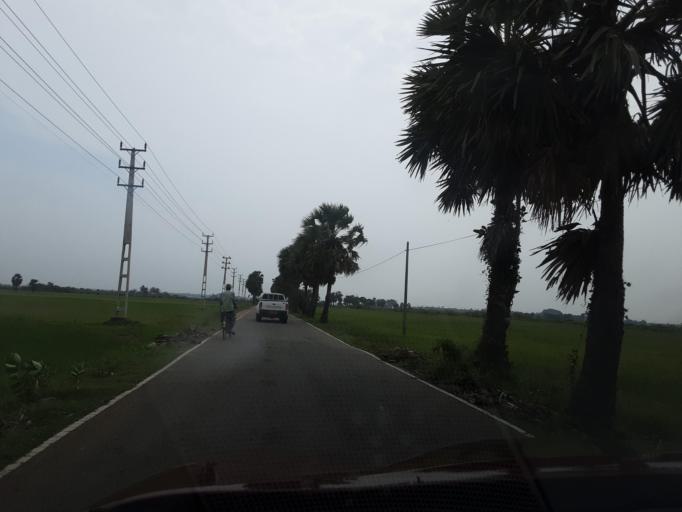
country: LK
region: Northern Province
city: Jaffna
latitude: 9.6667
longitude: 80.0562
